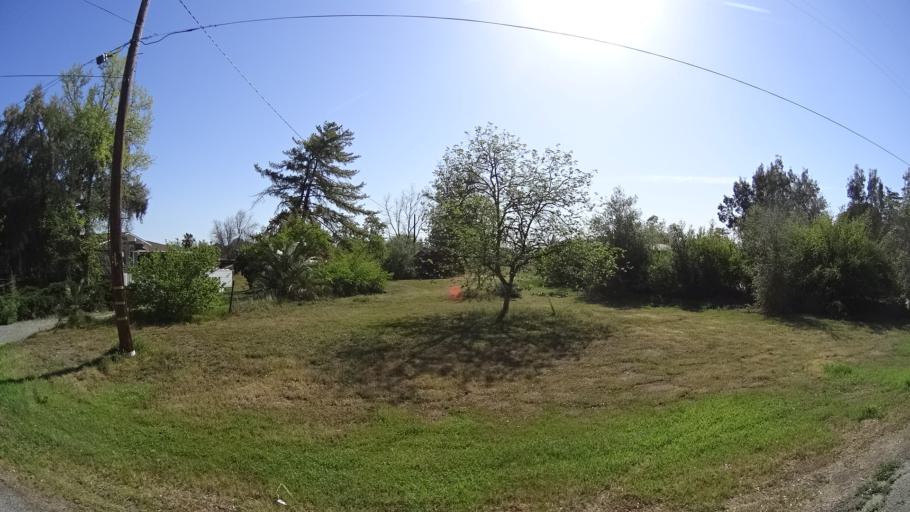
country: US
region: California
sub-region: Glenn County
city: Willows
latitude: 39.5351
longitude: -122.1983
